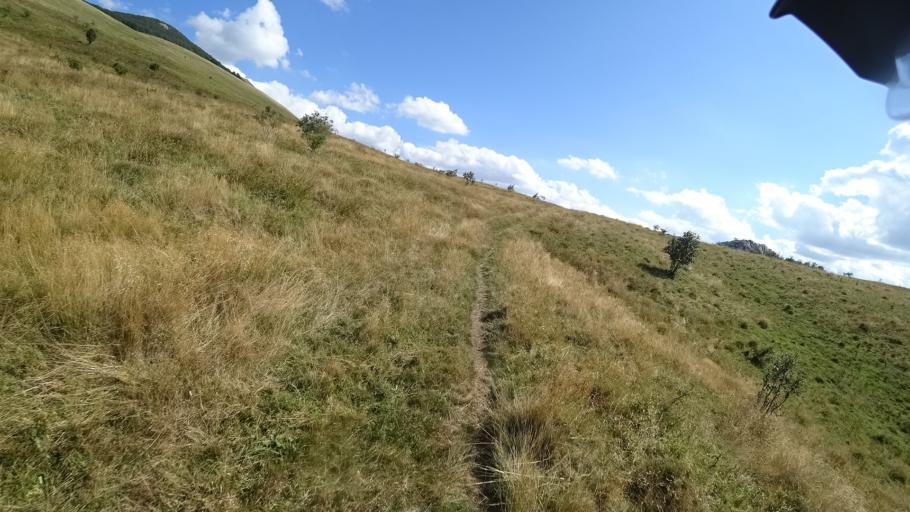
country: HR
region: Zadarska
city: Gracac
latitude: 44.4103
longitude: 16.0016
